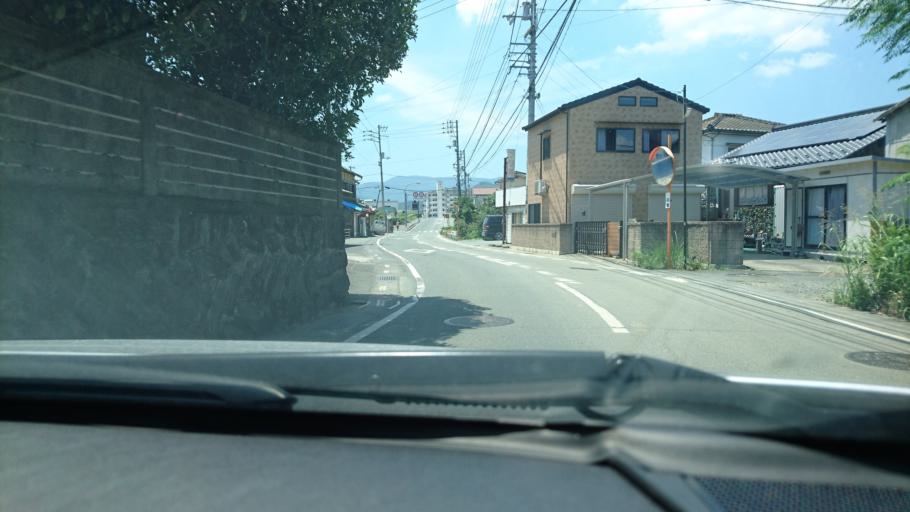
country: JP
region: Ehime
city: Ozu
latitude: 33.5077
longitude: 132.5376
